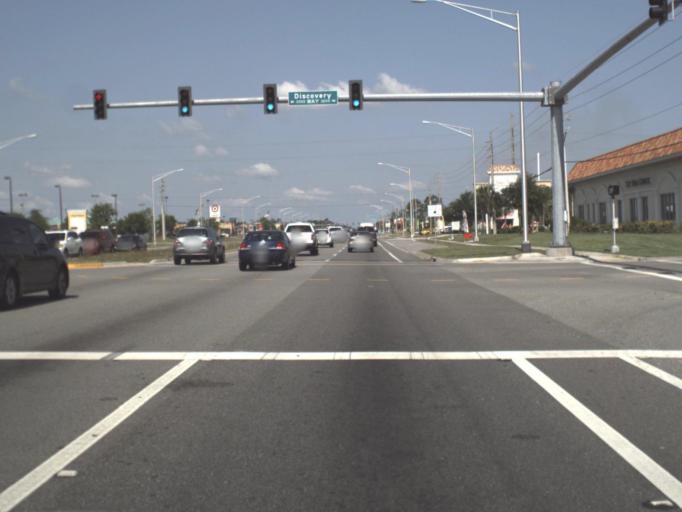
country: US
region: Florida
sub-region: Duval County
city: Jacksonville Beach
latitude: 30.2879
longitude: -81.4525
